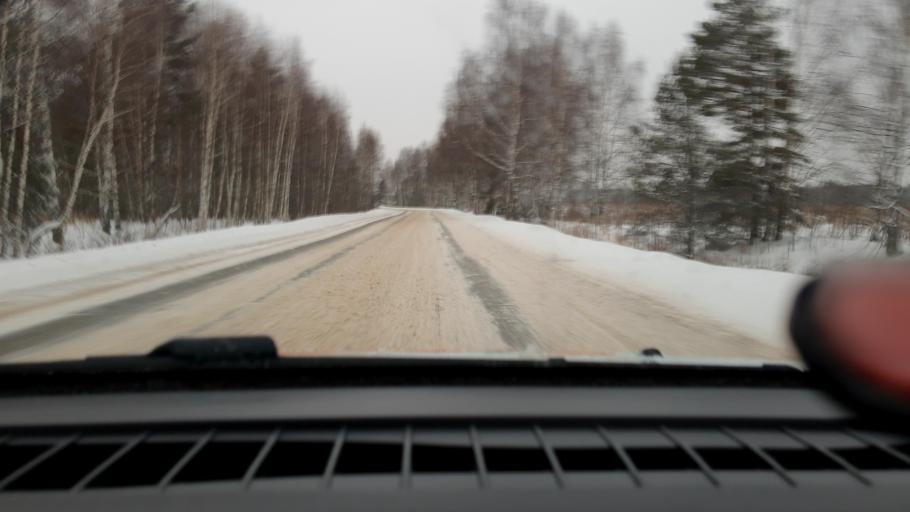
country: RU
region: Nizjnij Novgorod
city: Pamyat' Parizhskoy Kommuny
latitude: 56.2637
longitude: 44.4420
